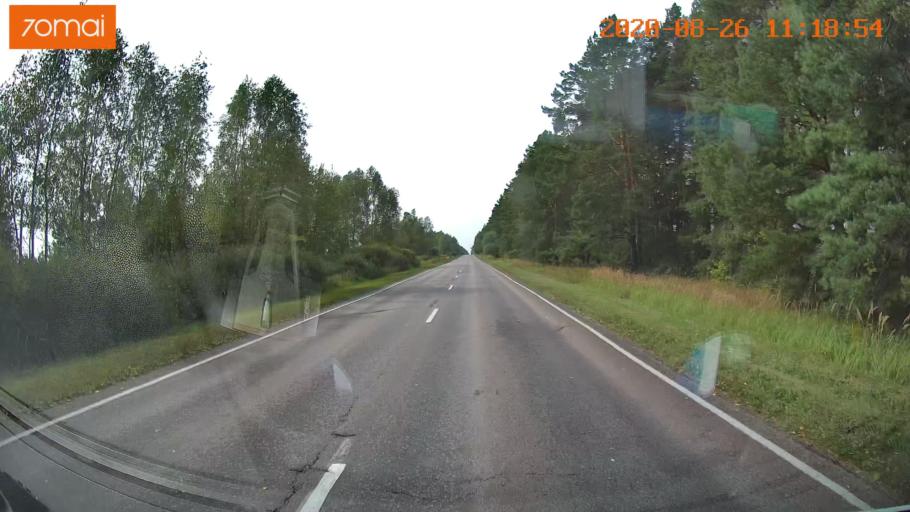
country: RU
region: Rjazan
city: Shilovo
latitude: 54.4053
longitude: 41.0891
